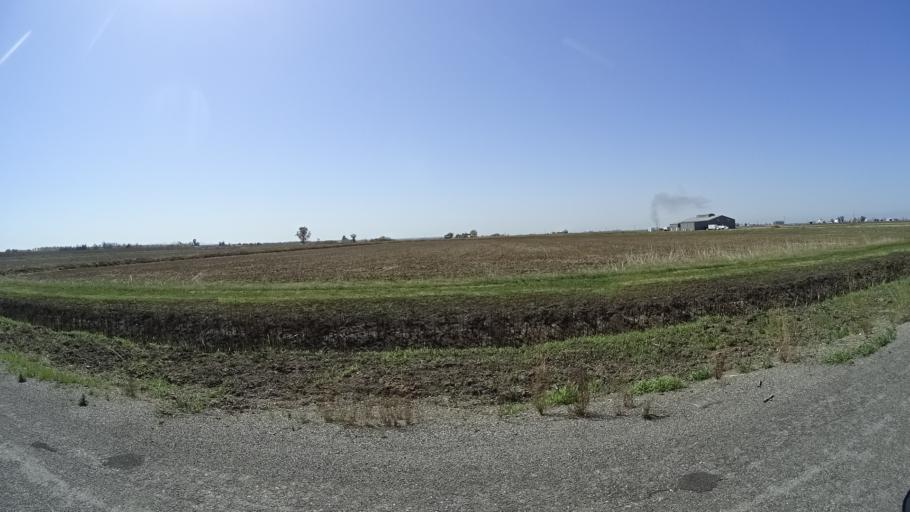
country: US
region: California
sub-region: Glenn County
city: Willows
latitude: 39.4431
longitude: -122.0282
